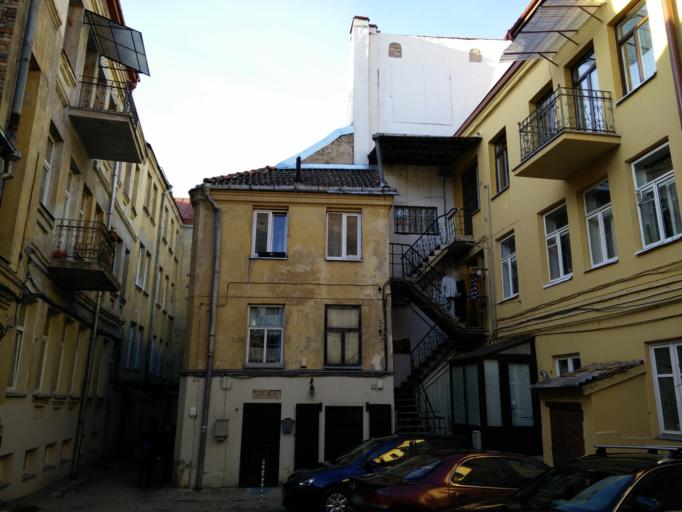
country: LT
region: Vilnius County
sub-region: Vilnius
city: Vilnius
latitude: 54.6834
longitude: 25.2876
